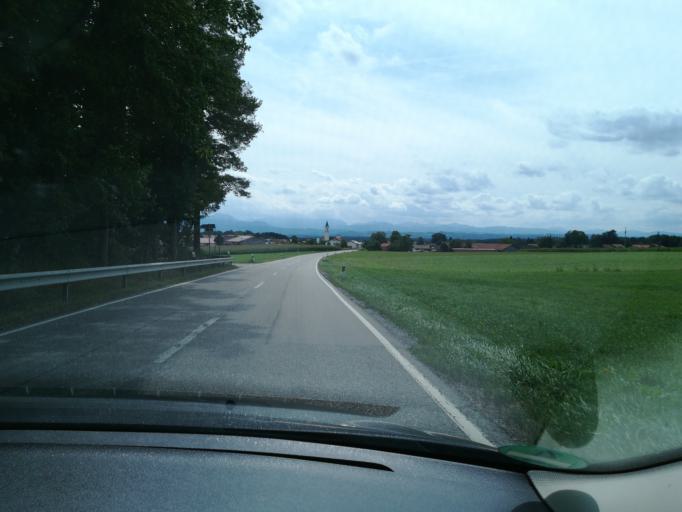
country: DE
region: Bavaria
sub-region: Upper Bavaria
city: Tuntenhausen
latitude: 47.9562
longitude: 11.9696
